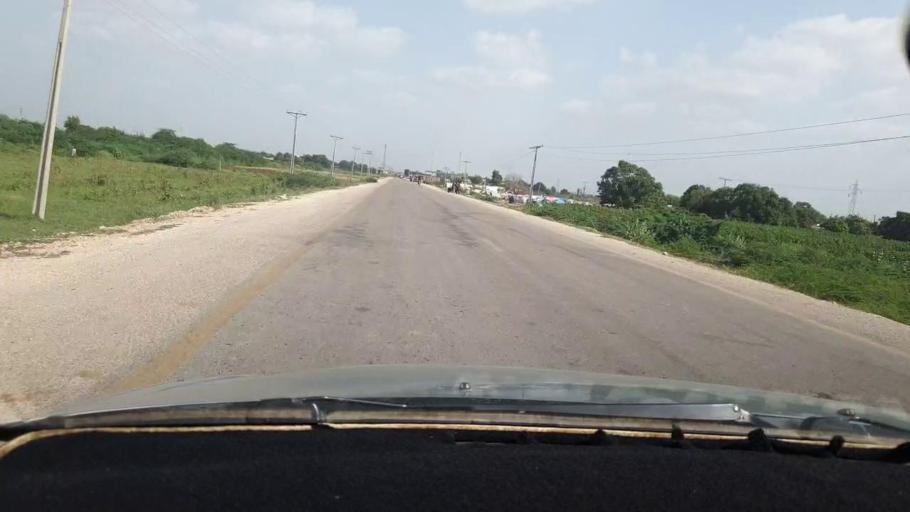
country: PK
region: Sindh
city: Naukot
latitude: 24.8623
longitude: 69.3896
